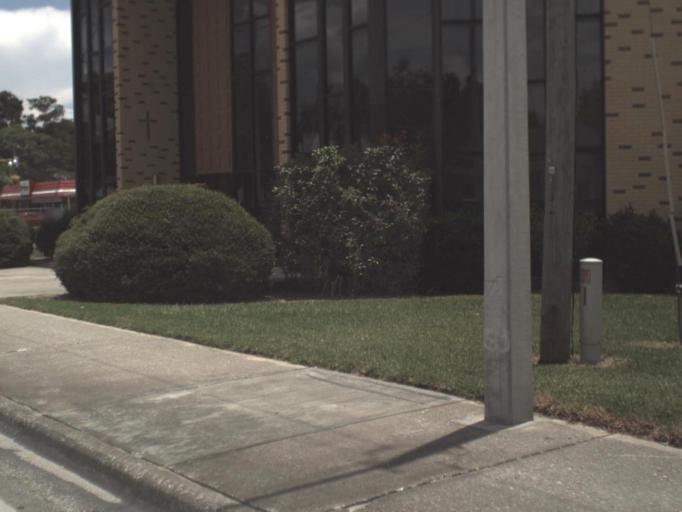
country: US
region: Florida
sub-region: Levy County
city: Williston
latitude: 29.3877
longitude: -82.4447
